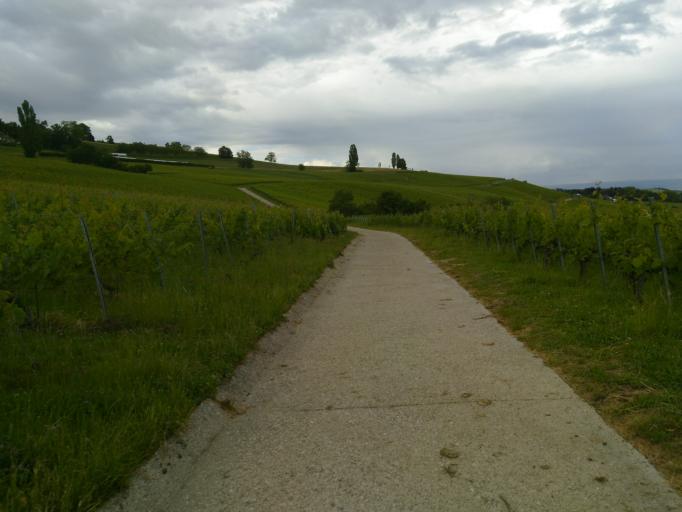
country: CH
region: Vaud
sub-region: Nyon District
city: Perroy
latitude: 46.4849
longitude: 6.3705
